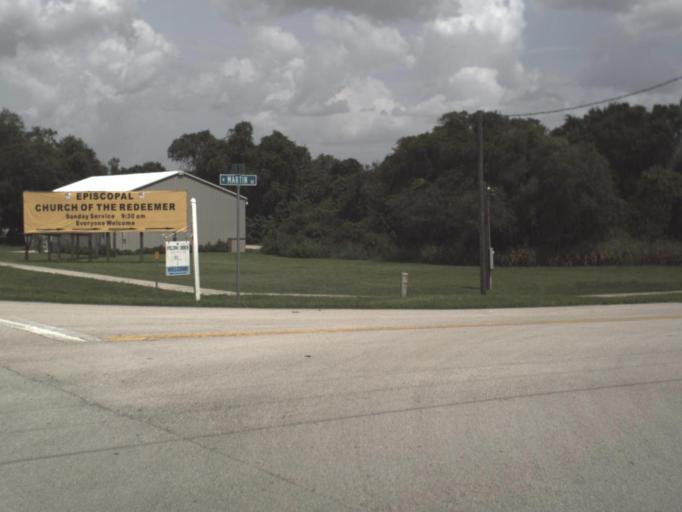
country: US
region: Florida
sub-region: Highlands County
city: Avon Park
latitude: 27.5736
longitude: -81.5143
